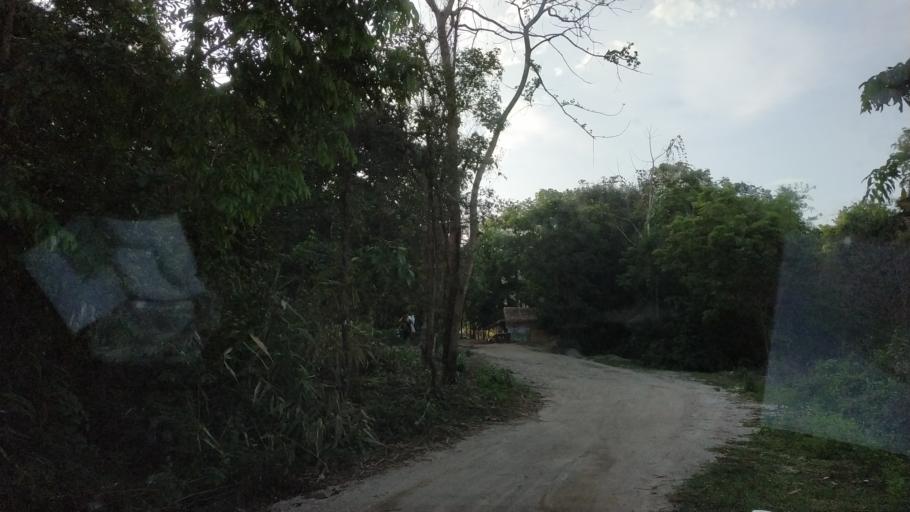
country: MM
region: Mon
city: Kyaikto
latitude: 17.4355
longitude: 97.0404
